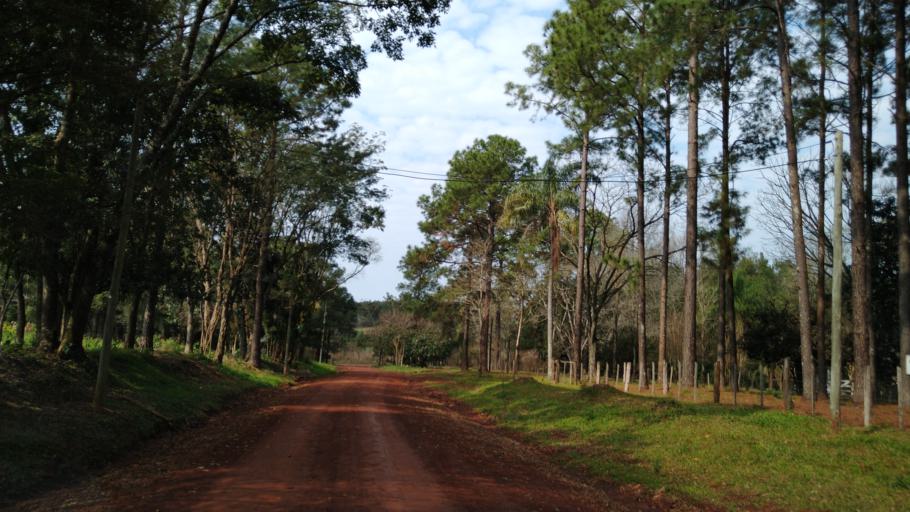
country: AR
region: Misiones
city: Ruiz de Montoya
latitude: -26.9608
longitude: -55.0576
